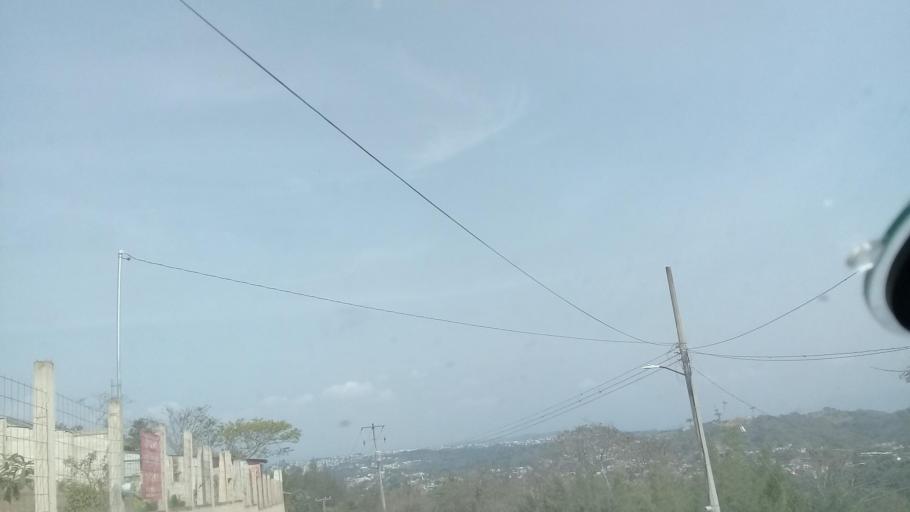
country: MX
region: Veracruz
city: El Castillo
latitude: 19.5364
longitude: -96.8529
